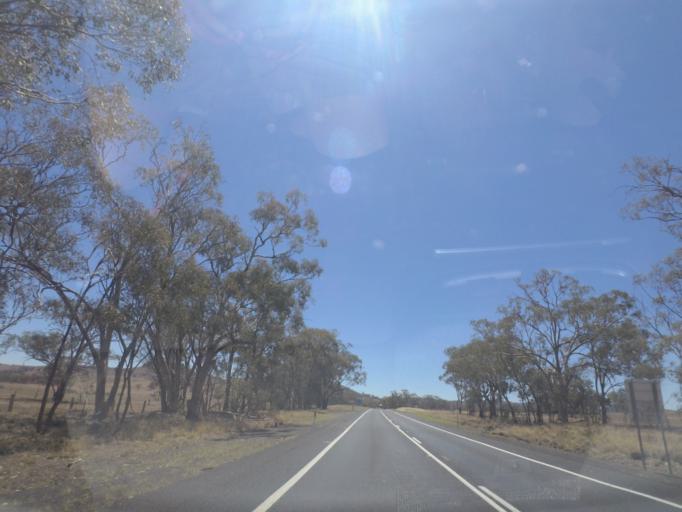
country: AU
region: New South Wales
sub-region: Warrumbungle Shire
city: Coonabarabran
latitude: -31.4460
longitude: 149.1210
